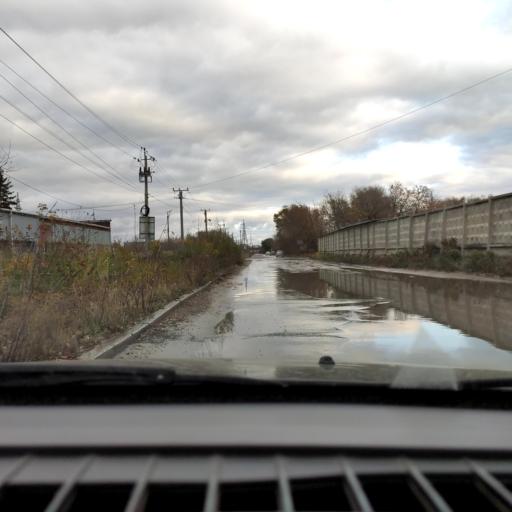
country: RU
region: Samara
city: Tol'yatti
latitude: 53.5704
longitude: 49.2859
